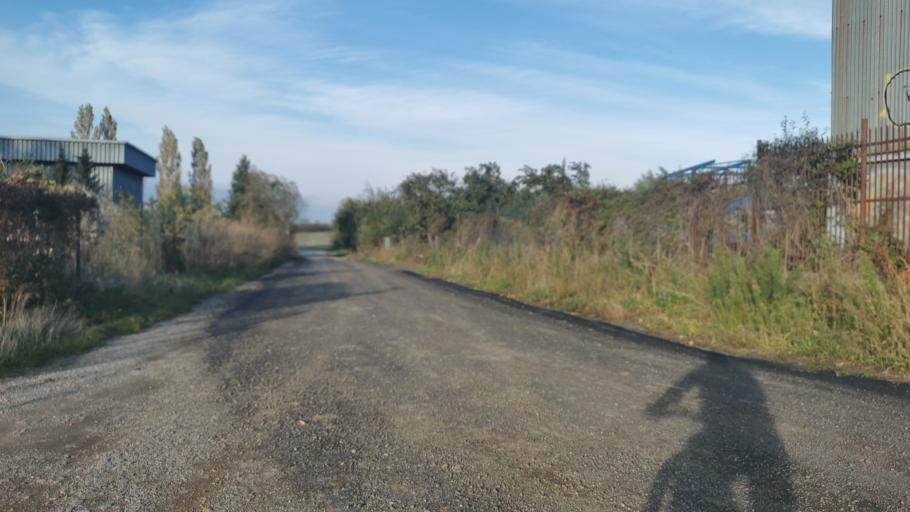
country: CZ
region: South Moravian
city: Sudomerice
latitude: 48.8458
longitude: 17.2549
